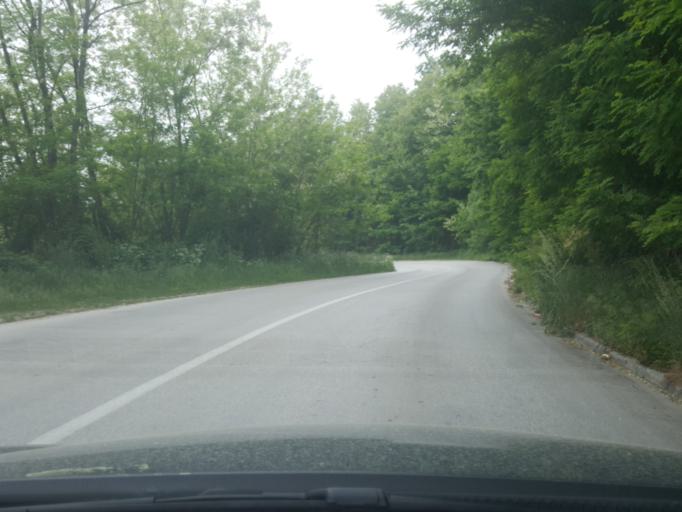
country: RS
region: Central Serbia
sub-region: Zlatiborski Okrug
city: Bajina Basta
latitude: 43.9445
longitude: 19.5593
